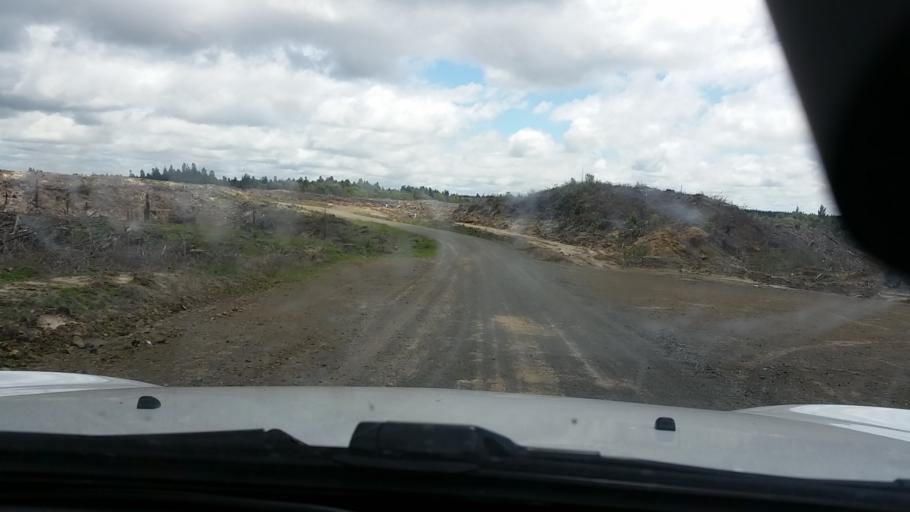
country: NZ
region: Bay of Plenty
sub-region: Kawerau District
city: Kawerau
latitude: -37.9998
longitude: 176.5459
